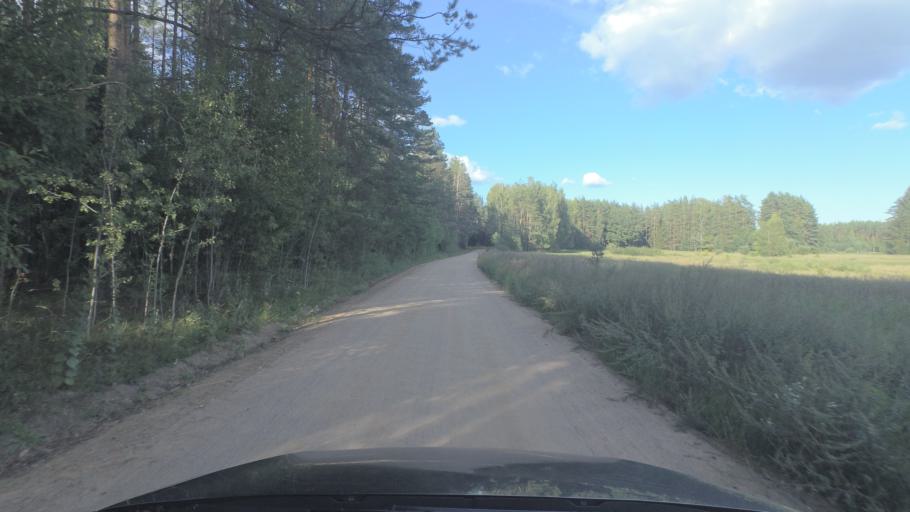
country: LT
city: Pabrade
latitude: 55.1472
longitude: 25.7479
